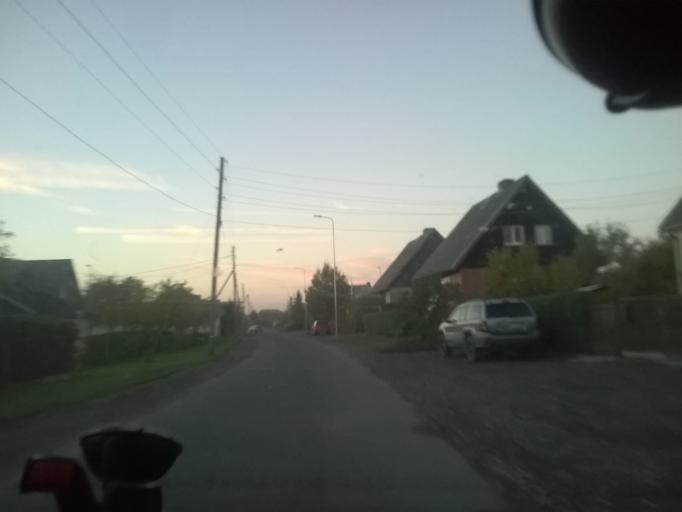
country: EE
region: Laeaene
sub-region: Haapsalu linn
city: Haapsalu
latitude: 58.9380
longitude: 23.5643
